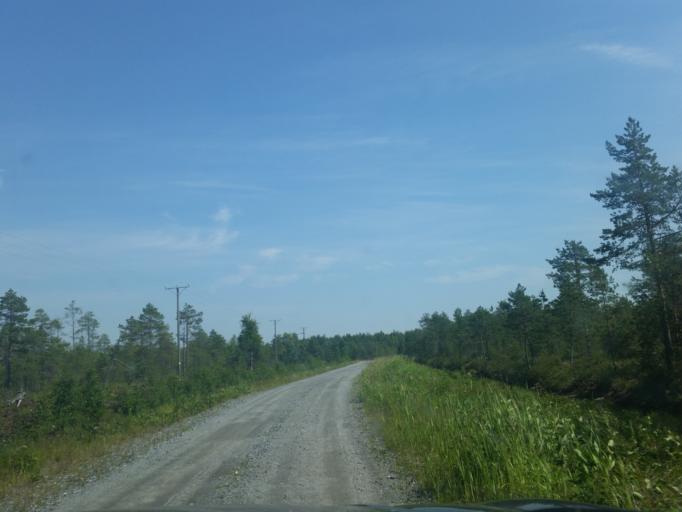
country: FI
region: Northern Savo
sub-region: Ylae-Savo
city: Keitele
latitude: 63.1011
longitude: 26.5512
